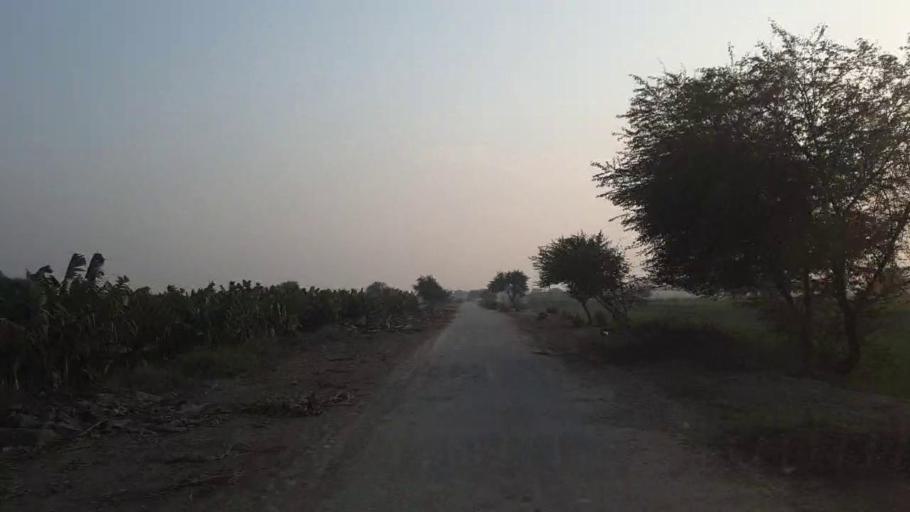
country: PK
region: Sindh
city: Bhit Shah
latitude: 25.7732
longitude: 68.4618
